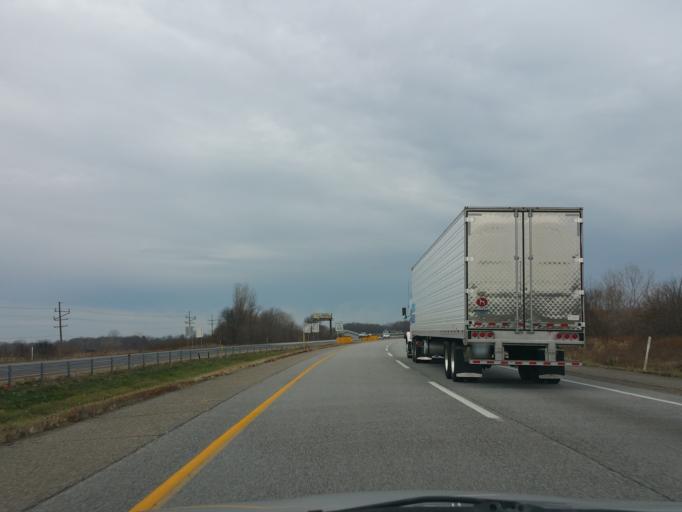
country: US
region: Indiana
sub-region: Porter County
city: Portage
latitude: 41.5721
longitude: -87.1478
